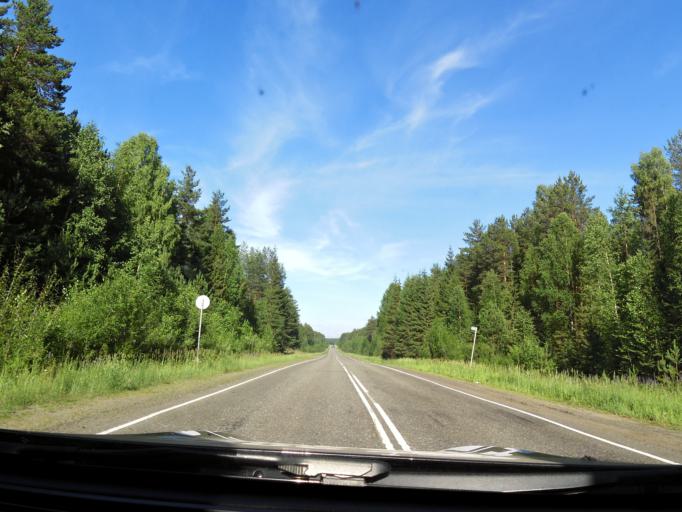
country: RU
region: Kirov
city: Dubrovka
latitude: 58.9060
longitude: 51.2220
